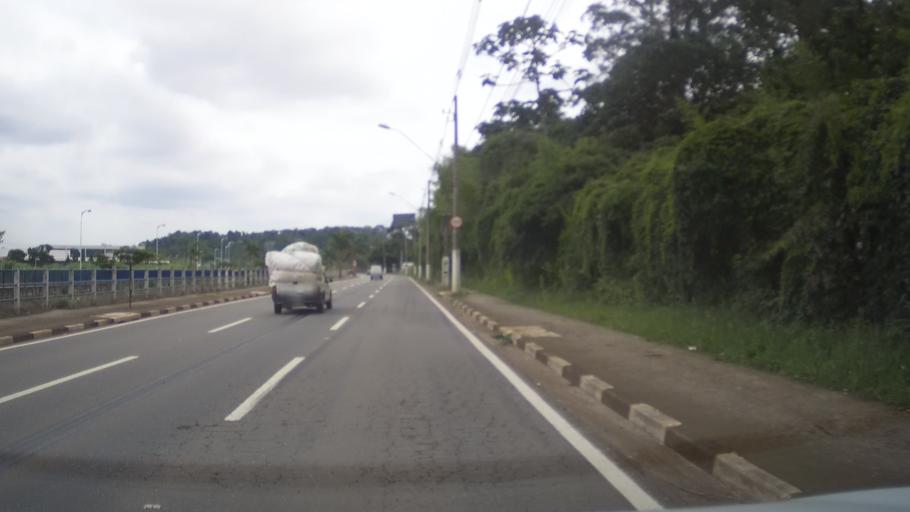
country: BR
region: Sao Paulo
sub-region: Aruja
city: Aruja
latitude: -23.4004
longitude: -46.3539
